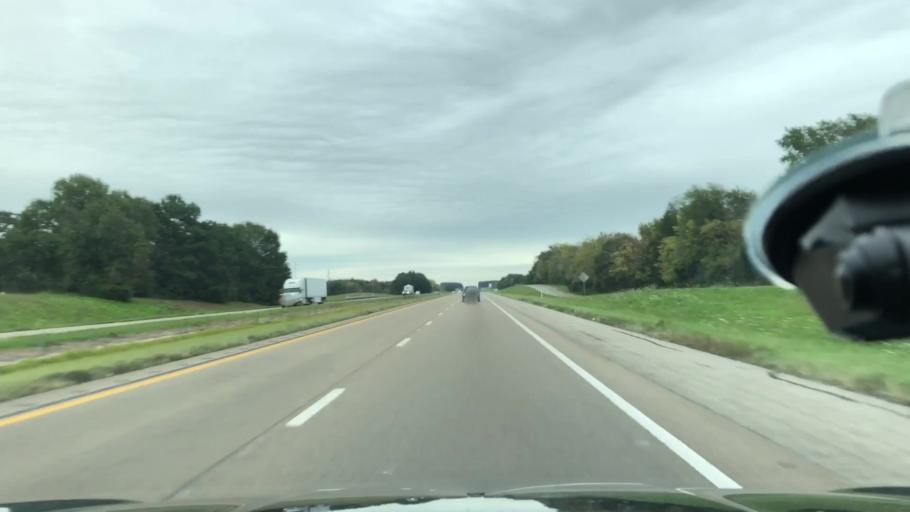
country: US
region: Texas
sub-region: Franklin County
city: Mount Vernon
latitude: 33.1599
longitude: -95.1005
